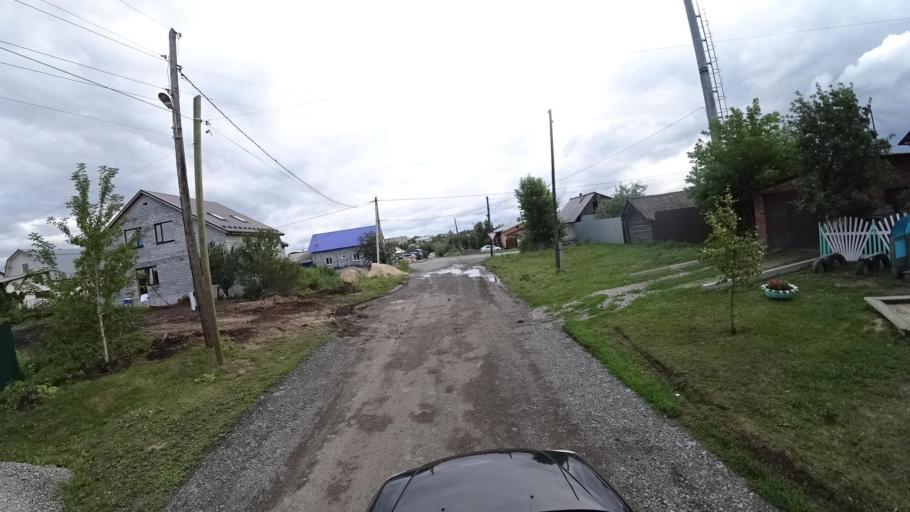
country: RU
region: Sverdlovsk
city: Kamyshlov
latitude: 56.8582
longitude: 62.7038
